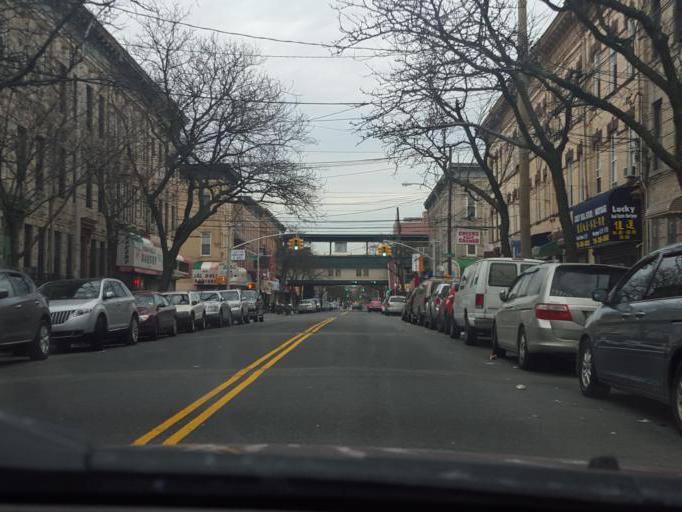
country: US
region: New York
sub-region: Kings County
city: East New York
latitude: 40.7037
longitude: -73.9091
